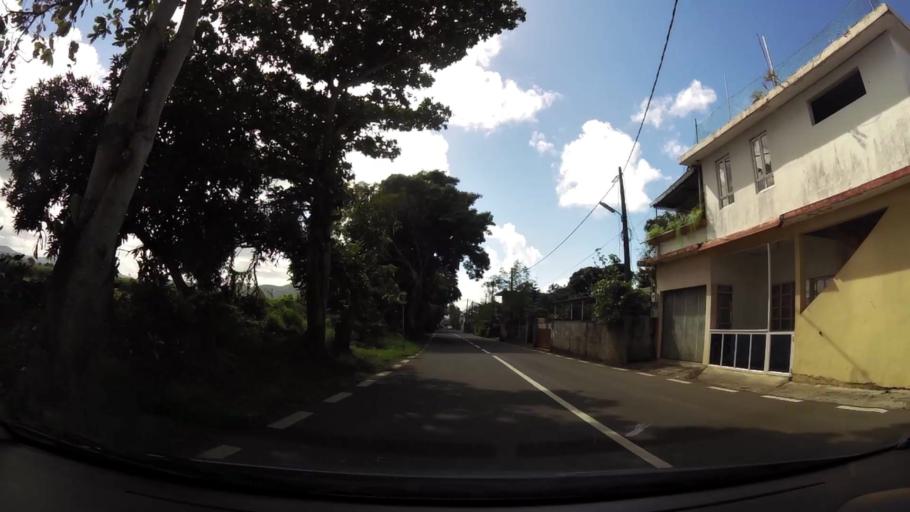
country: MU
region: Grand Port
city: Plaine Magnien
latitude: -20.4291
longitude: 57.6667
